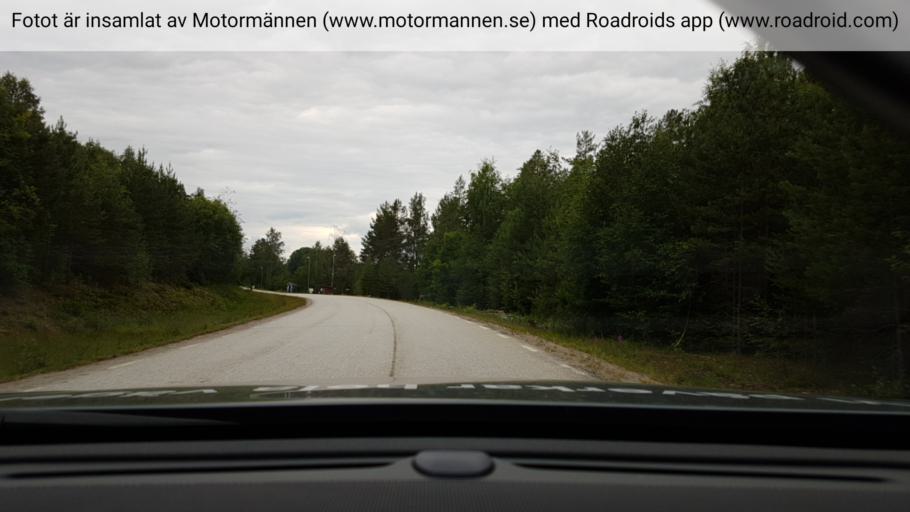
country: SE
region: Vaesterbotten
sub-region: Vannas Kommun
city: Vannasby
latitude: 64.0069
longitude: 19.9196
